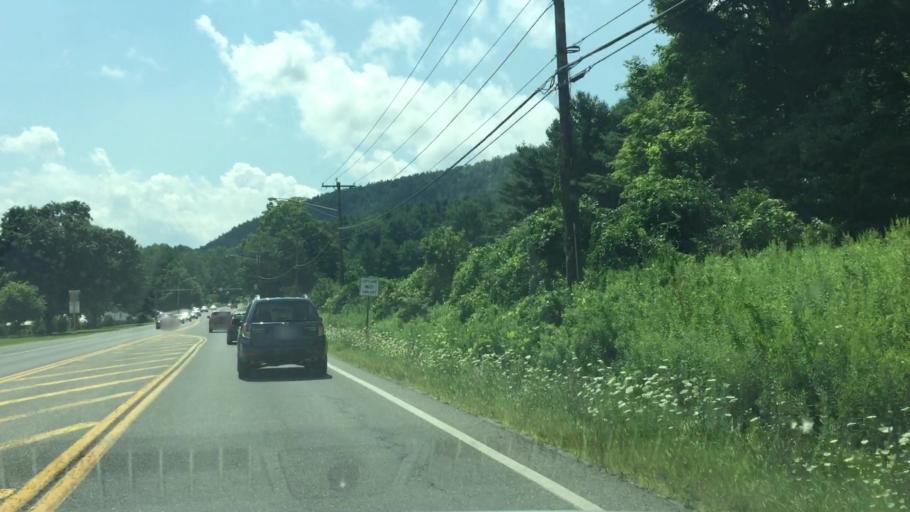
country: US
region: Massachusetts
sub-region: Berkshire County
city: Housatonic
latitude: 42.2505
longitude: -73.3307
